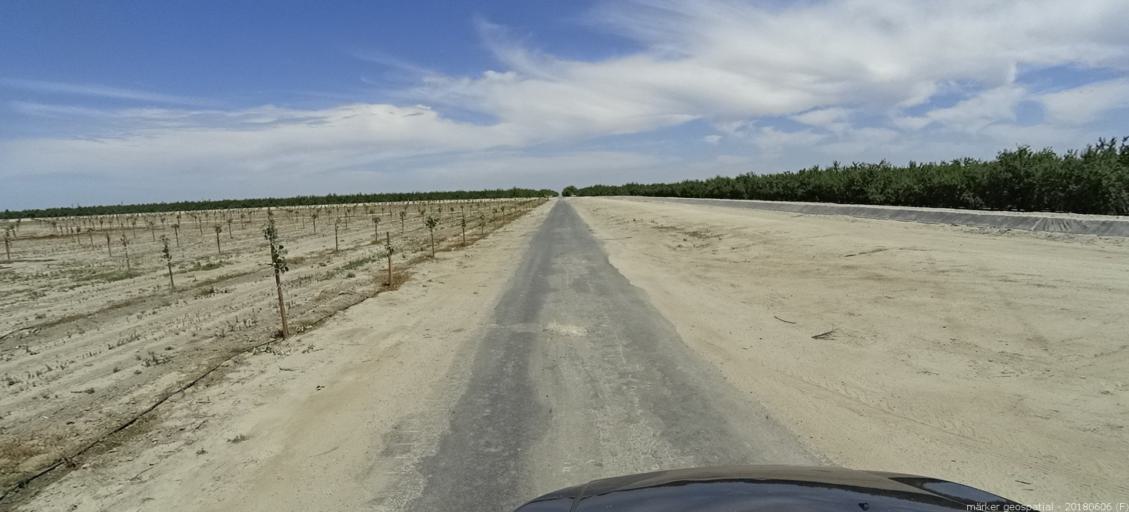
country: US
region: California
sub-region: Fresno County
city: Firebaugh
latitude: 36.8684
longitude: -120.3998
